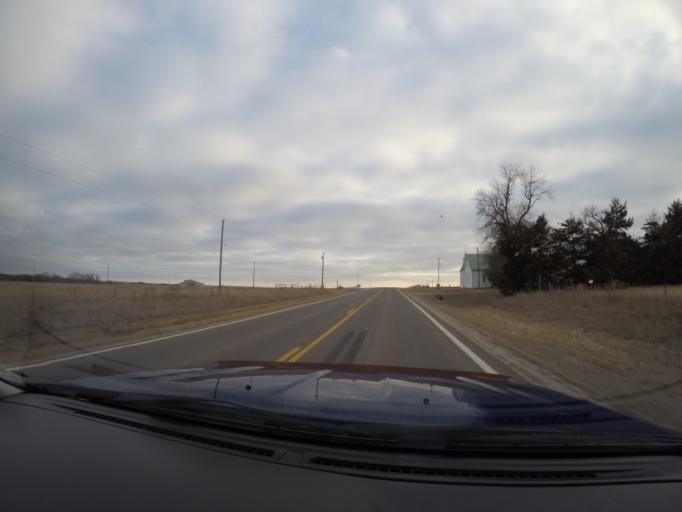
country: US
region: Kansas
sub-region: Morris County
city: Council Grove
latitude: 38.7834
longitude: -96.5013
